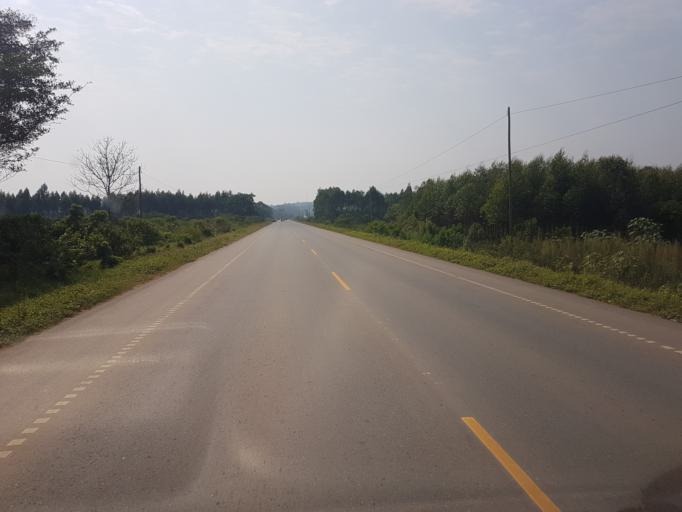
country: UG
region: Western Region
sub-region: Mbarara District
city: Bwizibwera
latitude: -0.6425
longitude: 30.5719
